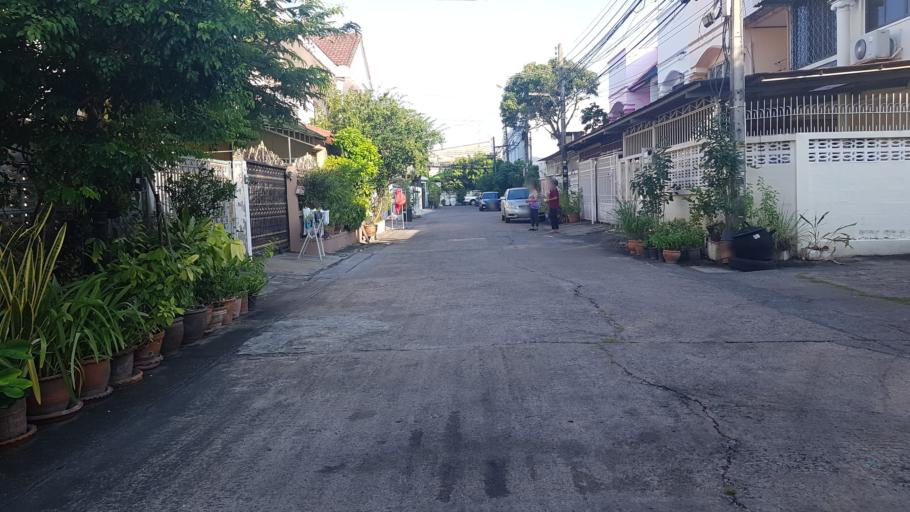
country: TH
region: Bangkok
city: Wang Thonglang
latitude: 13.7811
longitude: 100.6254
